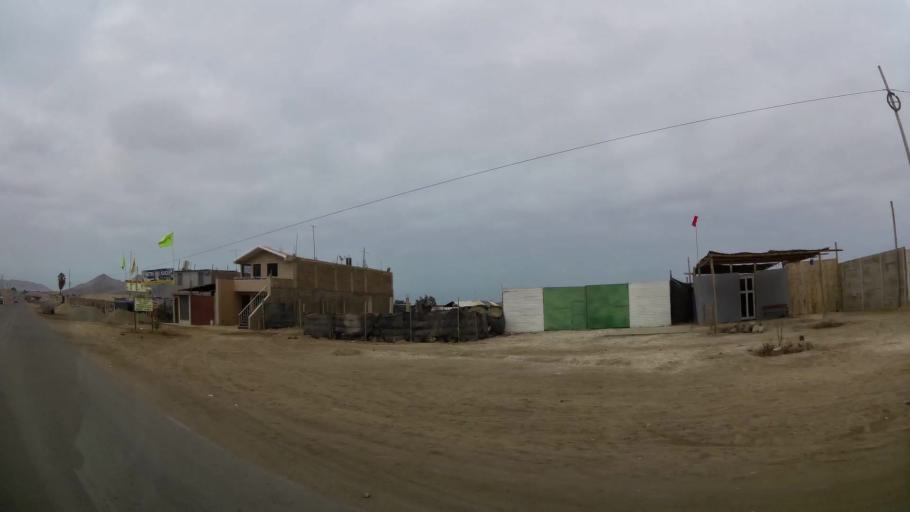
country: PE
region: Lima
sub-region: Provincia de Canete
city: Chilca
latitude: -12.5238
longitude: -76.7294
